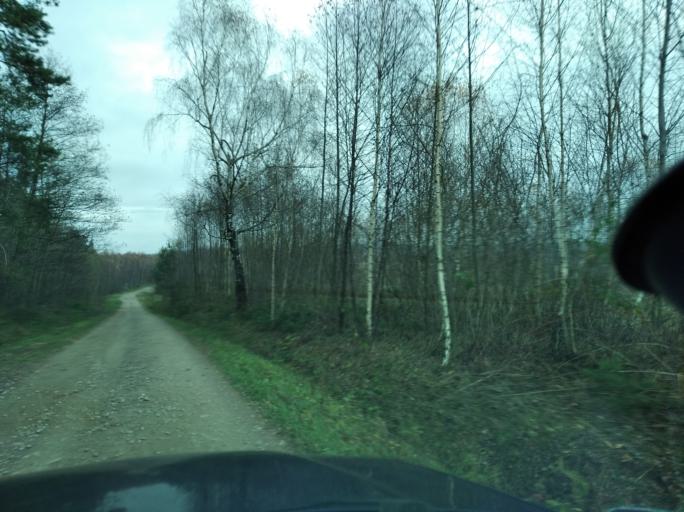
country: PL
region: Subcarpathian Voivodeship
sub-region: Powiat strzyzowski
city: Wysoka Strzyzowska
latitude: 49.7974
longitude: 21.7810
